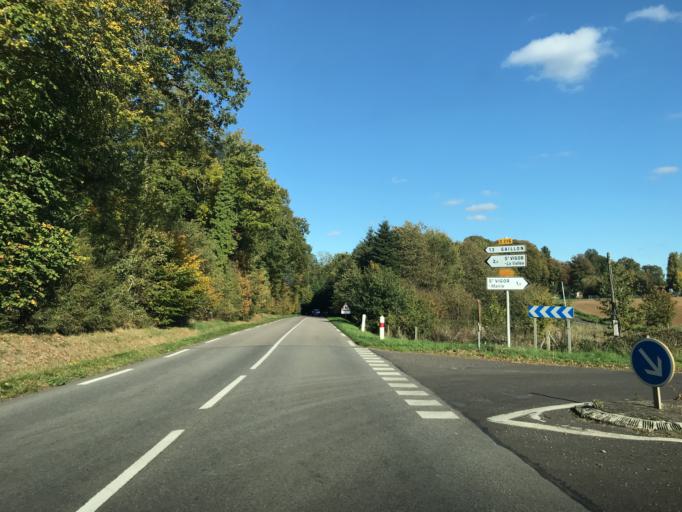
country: FR
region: Haute-Normandie
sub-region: Departement de l'Eure
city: Gravigny
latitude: 49.0769
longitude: 1.2460
